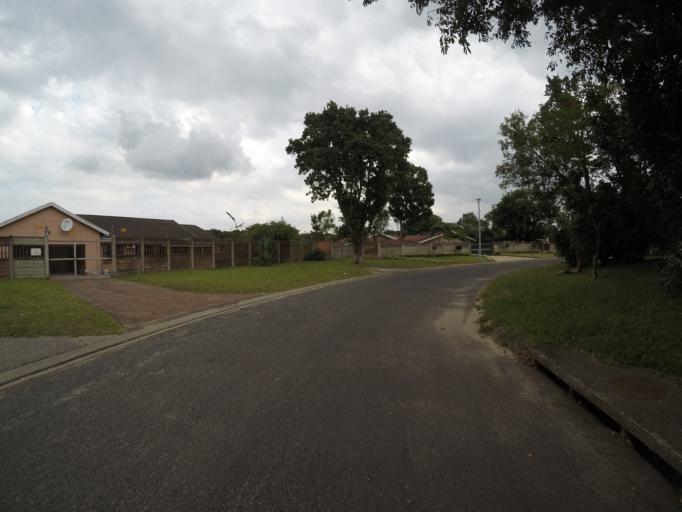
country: ZA
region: KwaZulu-Natal
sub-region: uThungulu District Municipality
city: Richards Bay
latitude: -28.7325
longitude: 32.0567
